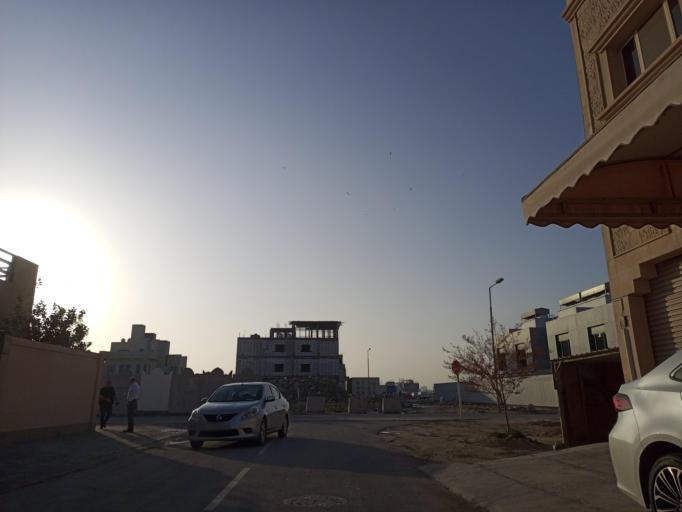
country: BH
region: Muharraq
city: Al Hadd
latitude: 26.2370
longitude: 50.6490
